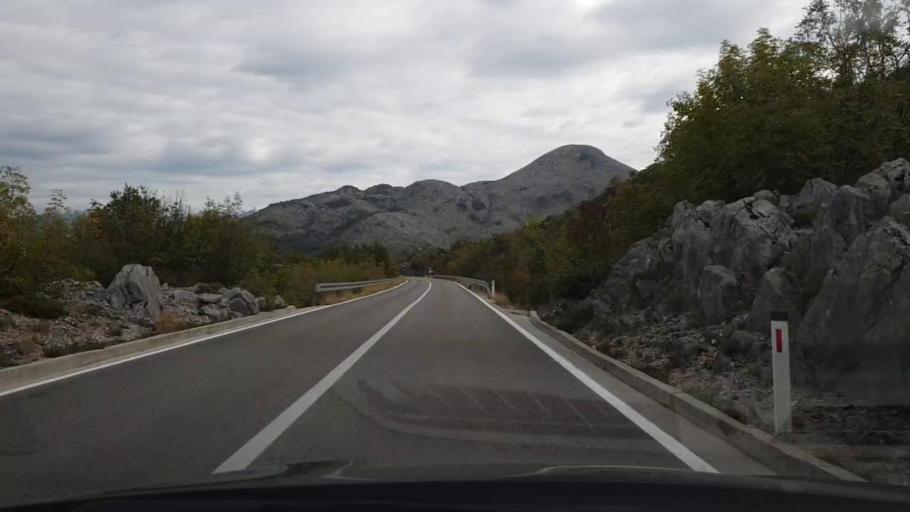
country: BA
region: Republika Srpska
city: Trebinje
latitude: 42.6900
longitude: 18.2759
